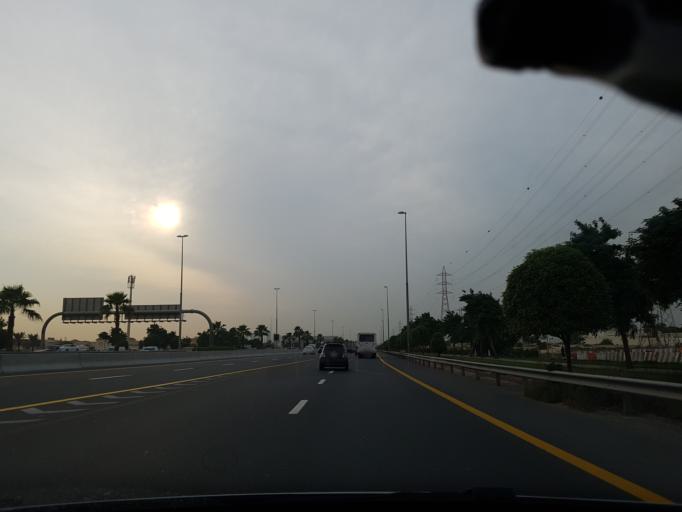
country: AE
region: Ash Shariqah
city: Sharjah
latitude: 25.2127
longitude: 55.3976
